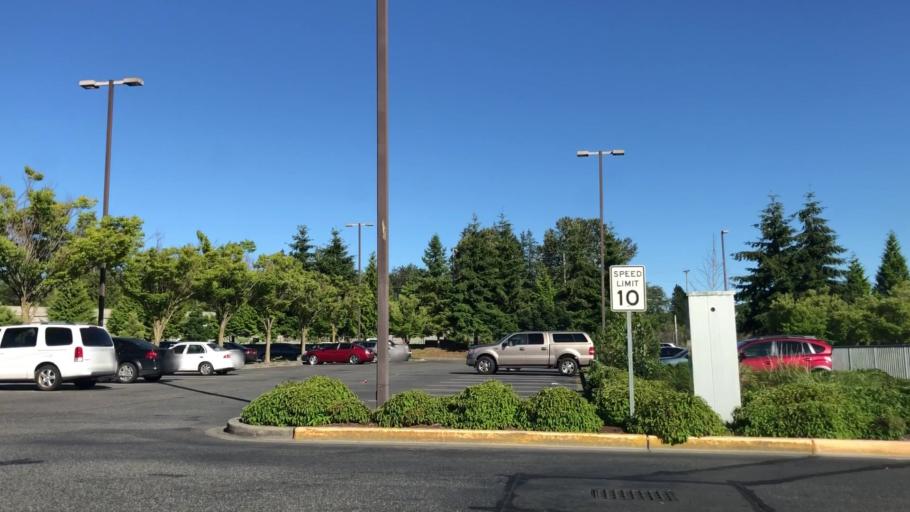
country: US
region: Washington
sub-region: Snohomish County
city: Martha Lake
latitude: 47.8523
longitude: -122.2587
